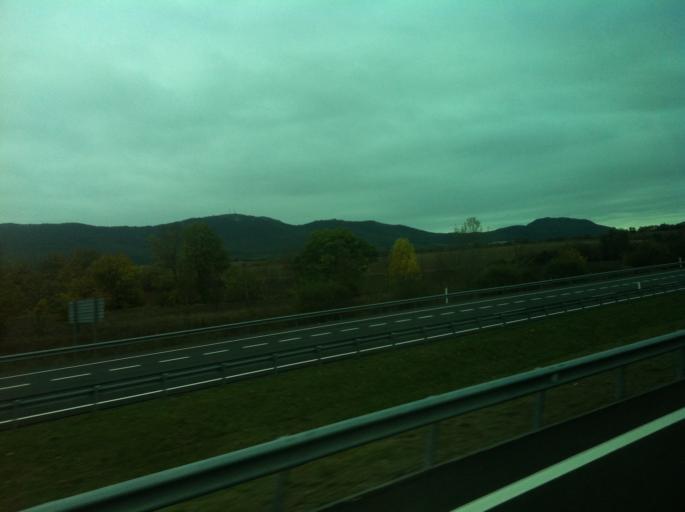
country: ES
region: Basque Country
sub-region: Provincia de Alava
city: Gasteiz / Vitoria
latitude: 42.8250
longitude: -2.7590
